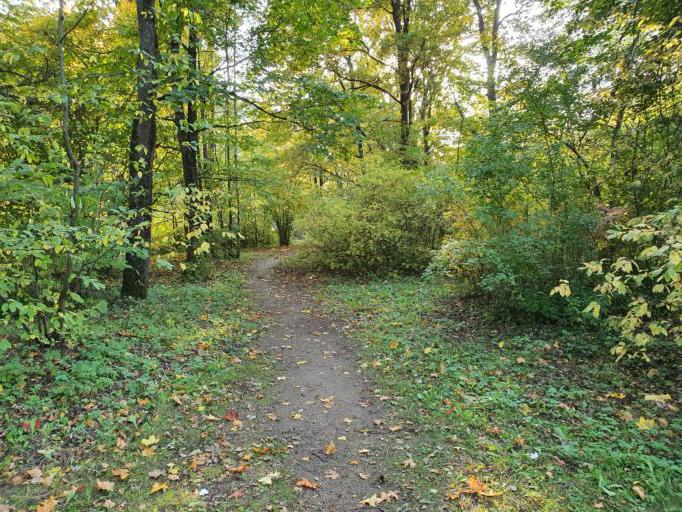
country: RU
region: St.-Petersburg
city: Pavlovsk
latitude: 59.6881
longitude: 30.4483
